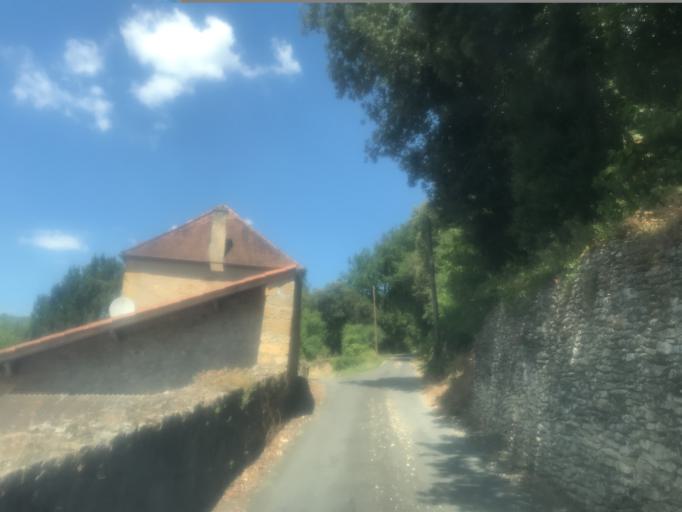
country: FR
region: Aquitaine
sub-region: Departement de la Dordogne
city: Cenac-et-Saint-Julien
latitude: 44.8202
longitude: 1.1932
